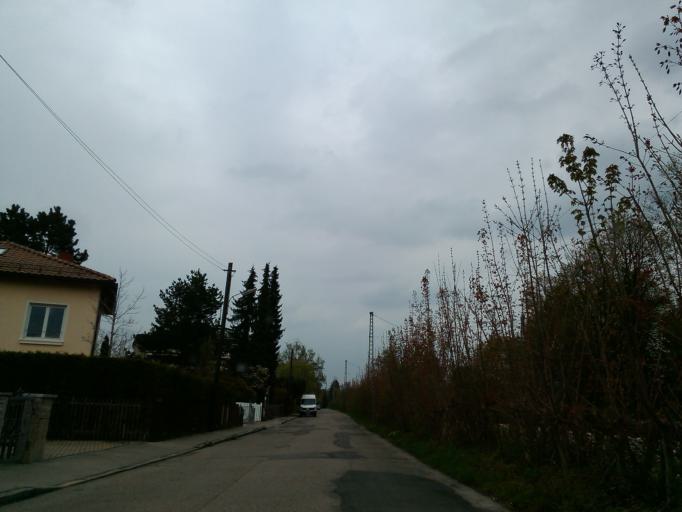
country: DE
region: Bavaria
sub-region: Upper Bavaria
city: Krailling
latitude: 48.0958
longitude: 11.4039
